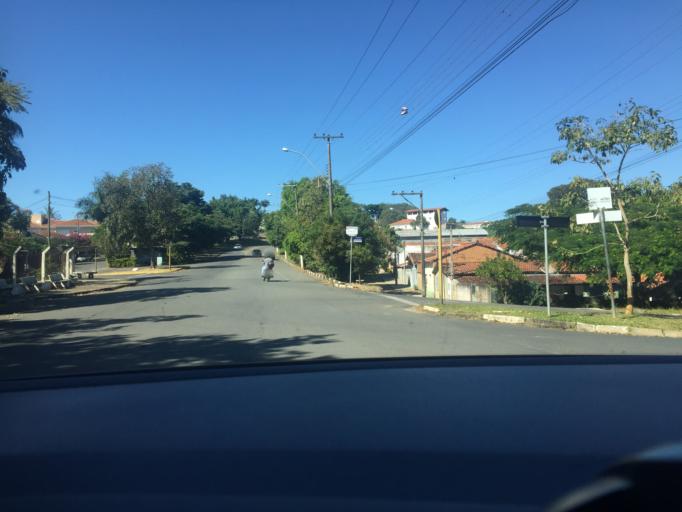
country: BR
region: Sao Paulo
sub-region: Santo Antonio Do Jardim
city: Espirito Santo do Pinhal
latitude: -22.1799
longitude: -46.7448
